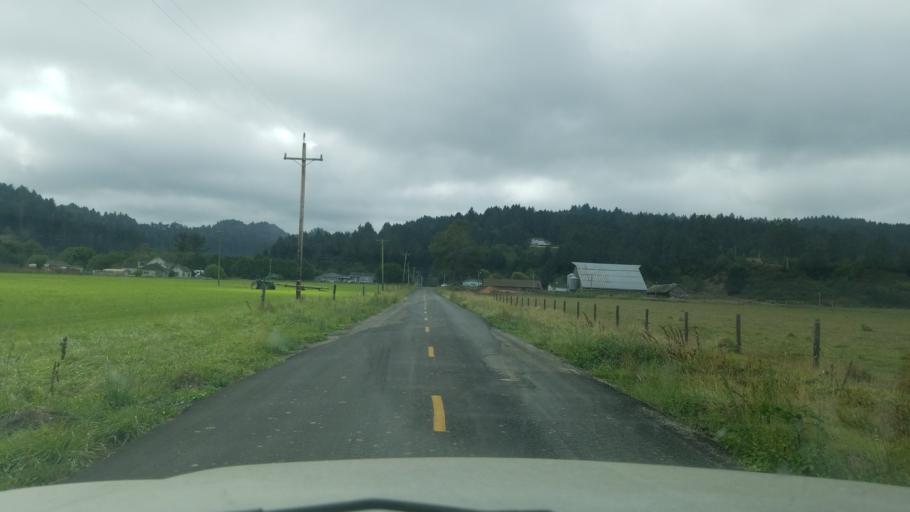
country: US
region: California
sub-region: Humboldt County
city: Ferndale
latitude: 40.5870
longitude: -124.2839
